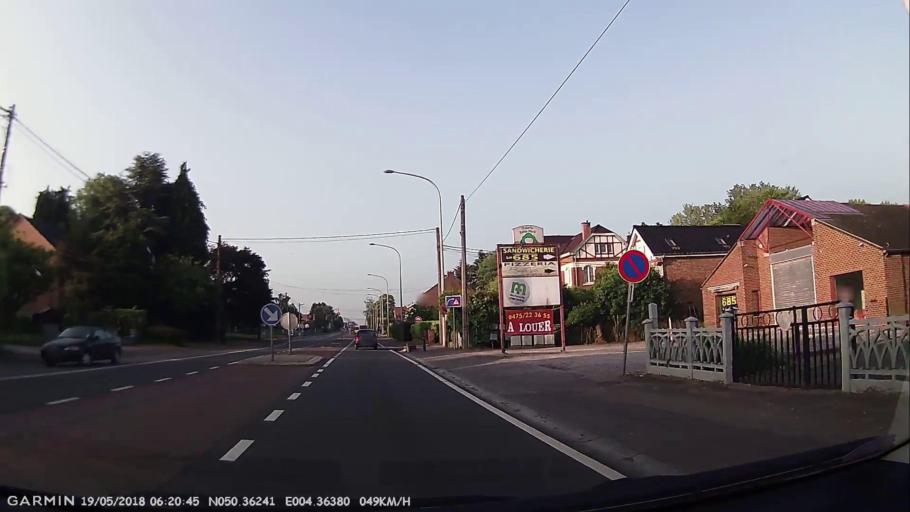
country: BE
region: Wallonia
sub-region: Province du Hainaut
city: Thuin
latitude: 50.3623
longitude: 4.3638
